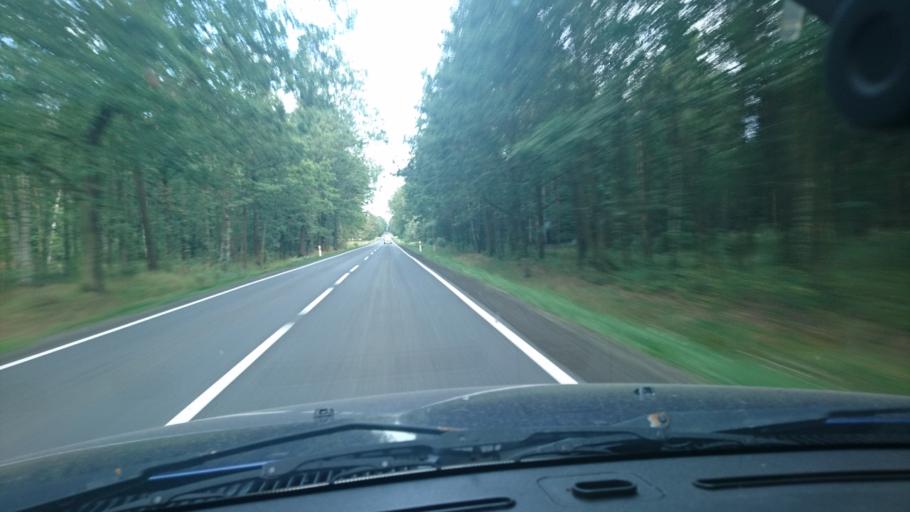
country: PL
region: Opole Voivodeship
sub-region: Powiat oleski
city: Olesno
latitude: 50.8488
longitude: 18.4748
